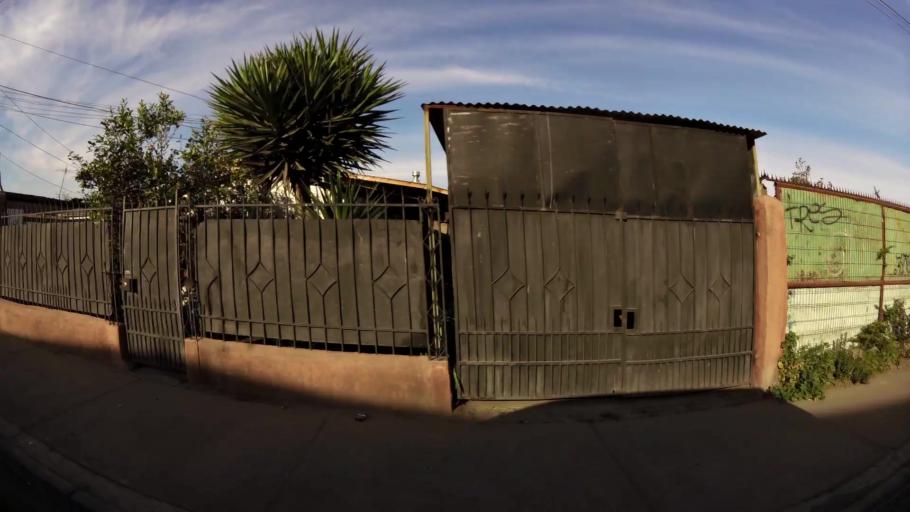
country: CL
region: Santiago Metropolitan
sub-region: Provincia de Cordillera
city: Puente Alto
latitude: -33.6138
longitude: -70.5784
